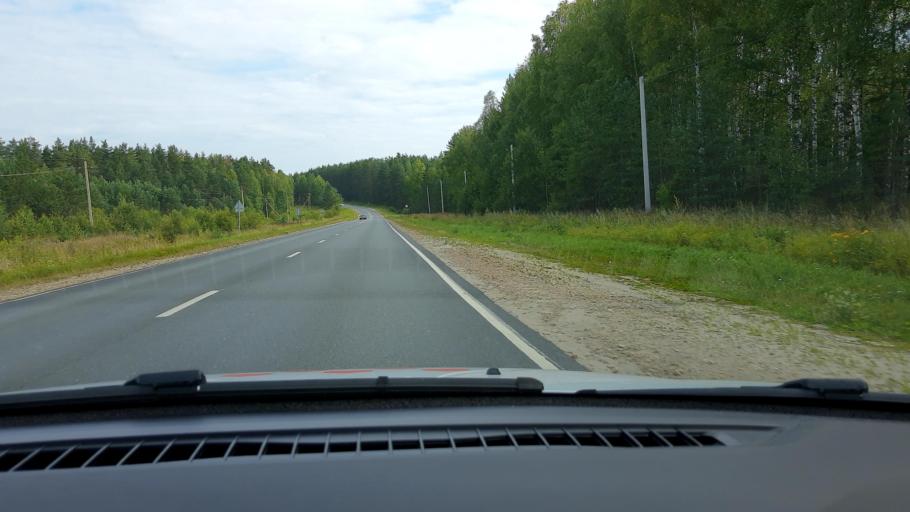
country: RU
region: Nizjnij Novgorod
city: Krasnyye Baki
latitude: 57.0184
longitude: 45.1168
